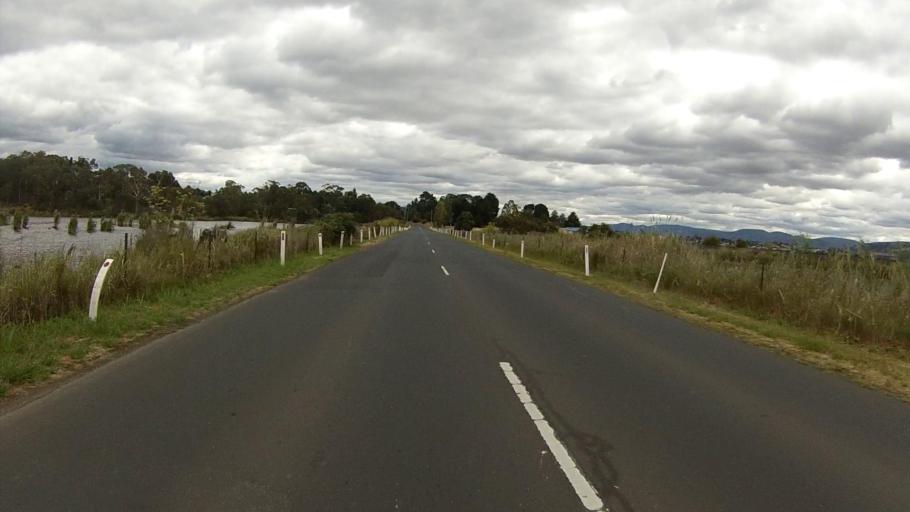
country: AU
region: Tasmania
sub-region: Glenorchy
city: Austins Ferry
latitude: -42.7649
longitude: 147.2427
